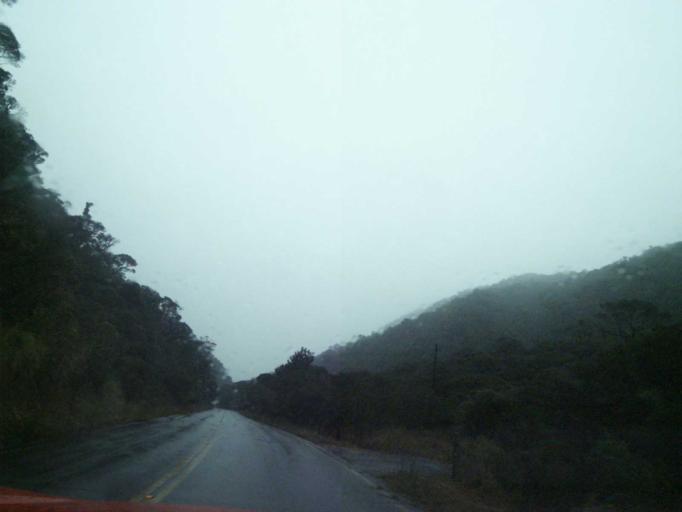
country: BR
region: Santa Catarina
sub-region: Anitapolis
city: Anitapolis
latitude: -27.7624
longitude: -49.0388
